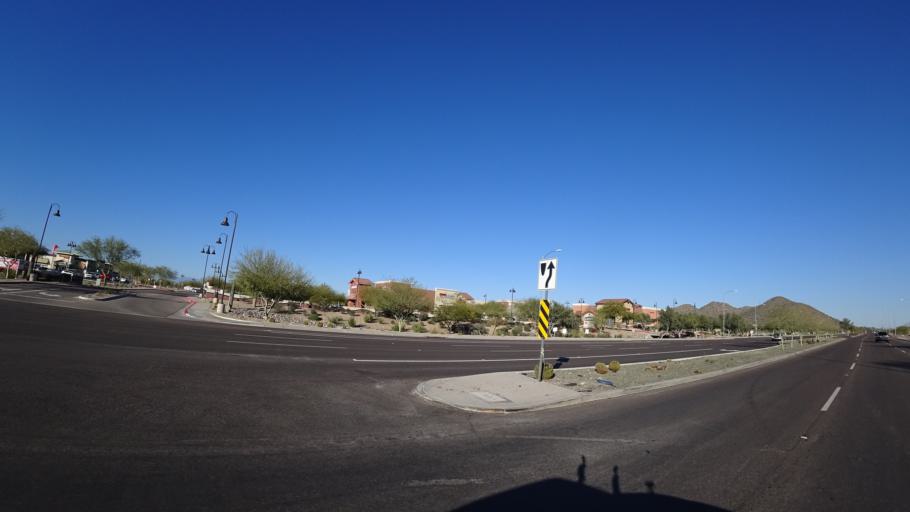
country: US
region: Arizona
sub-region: Maricopa County
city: Sun City West
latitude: 33.7106
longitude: -112.2699
